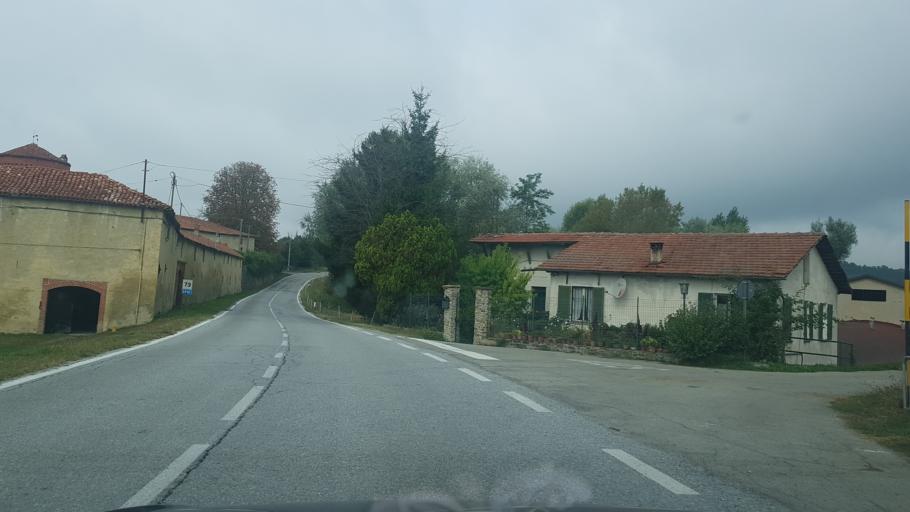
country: IT
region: Piedmont
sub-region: Provincia di Cuneo
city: Camerana
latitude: 44.4032
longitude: 8.1152
